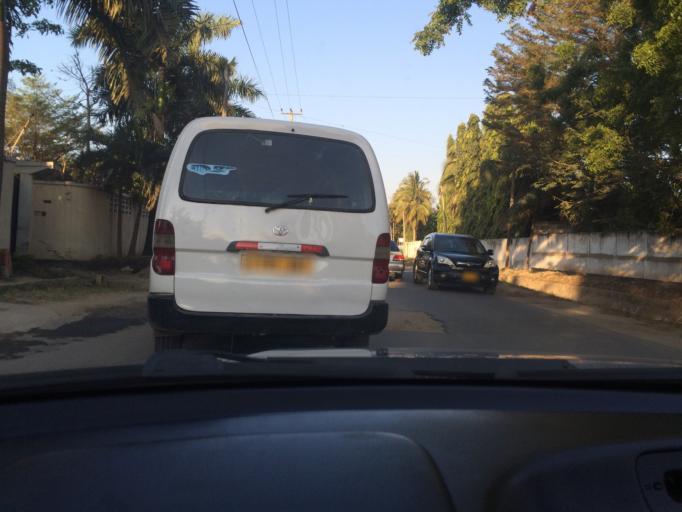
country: TZ
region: Dar es Salaam
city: Magomeni
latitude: -6.7722
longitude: 39.2586
